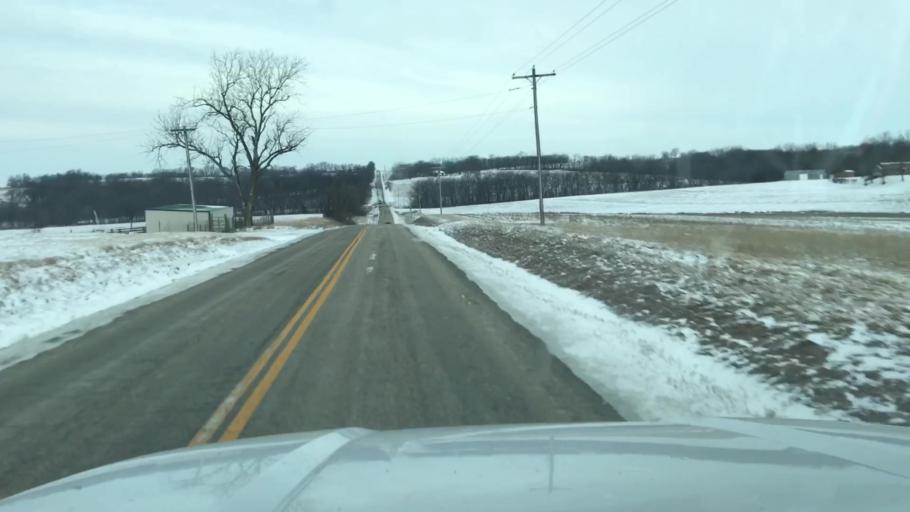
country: US
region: Missouri
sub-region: Holt County
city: Oregon
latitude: 40.1007
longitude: -94.9975
